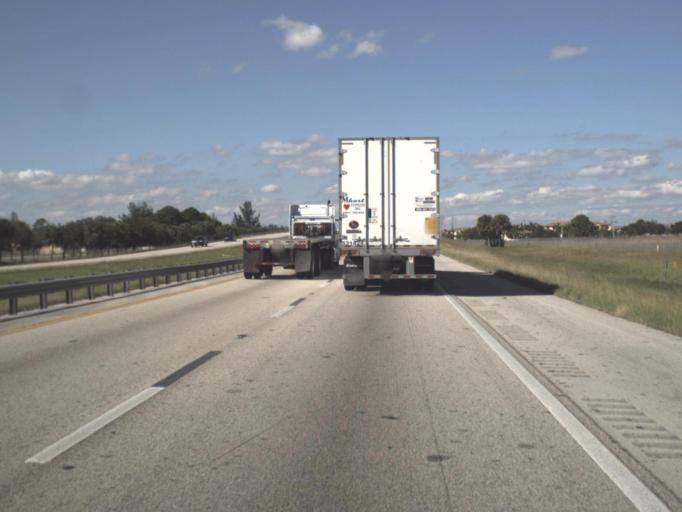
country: US
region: Florida
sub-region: Miami-Dade County
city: Lake Lucerne
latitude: 25.9722
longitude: -80.2579
